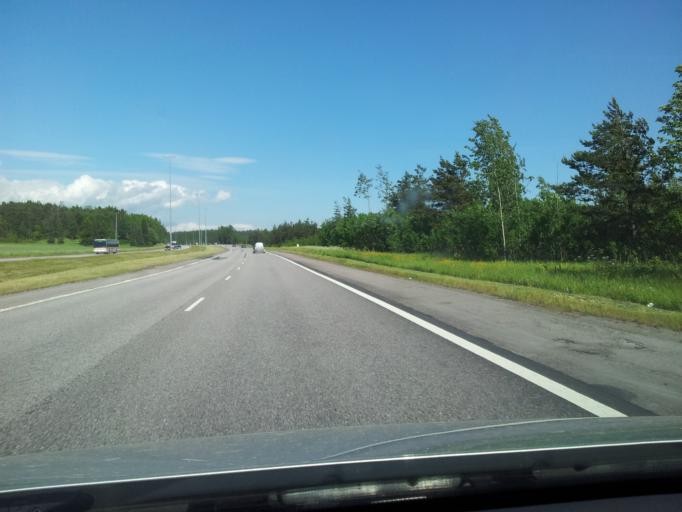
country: FI
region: Uusimaa
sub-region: Porvoo
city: Porvoo
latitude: 60.3577
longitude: 25.5351
